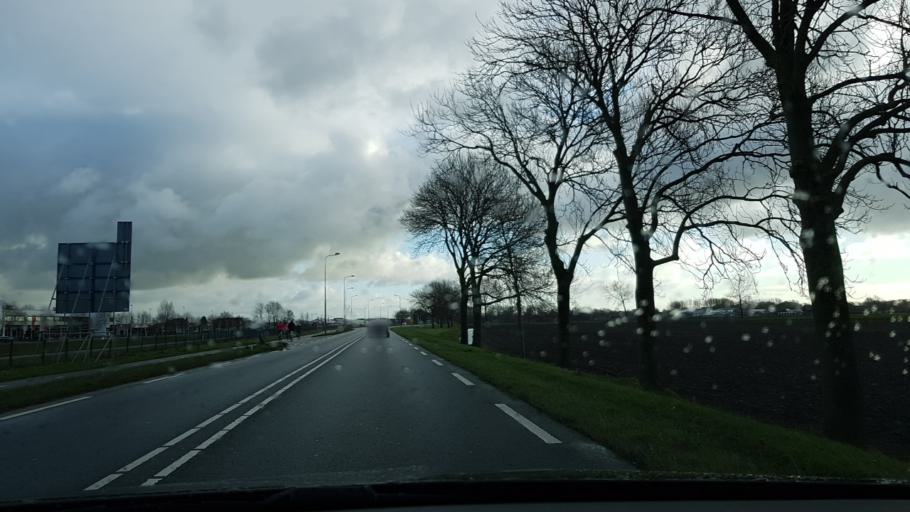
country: NL
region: North Holland
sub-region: Gemeente Aalsmeer
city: Aalsmeer
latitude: 52.2522
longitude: 4.7871
